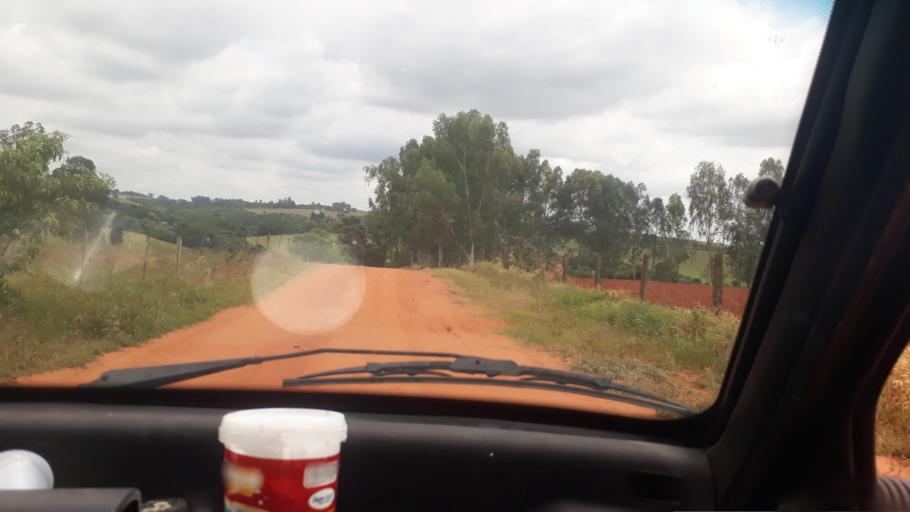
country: BR
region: Sao Paulo
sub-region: Regente Feijo
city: Regente Feijo
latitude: -22.2469
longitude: -51.2972
